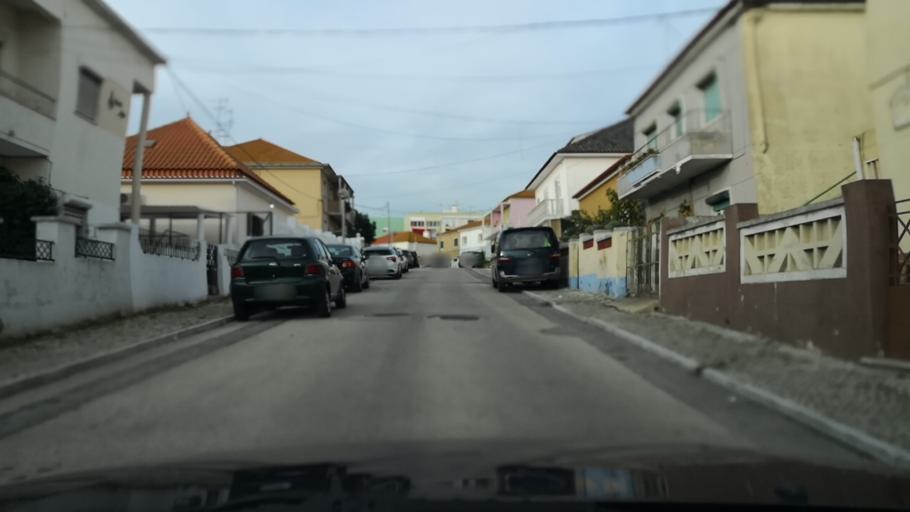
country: PT
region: Setubal
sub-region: Setubal
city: Setubal
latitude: 38.5236
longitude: -8.8758
